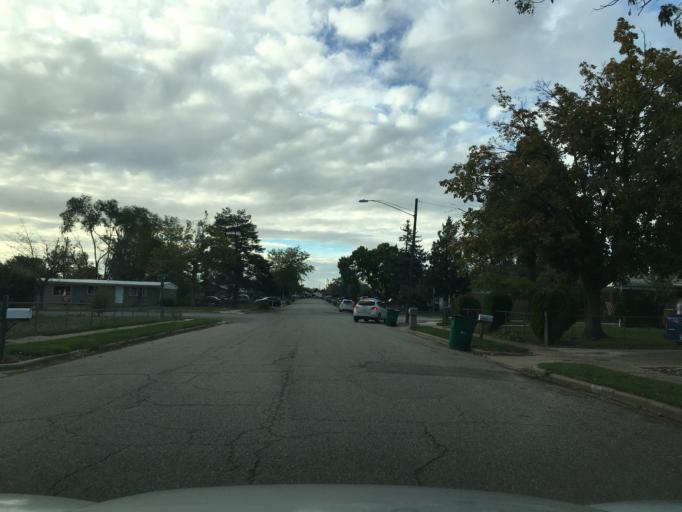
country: US
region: Utah
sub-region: Davis County
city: Layton
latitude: 41.0790
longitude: -111.9913
